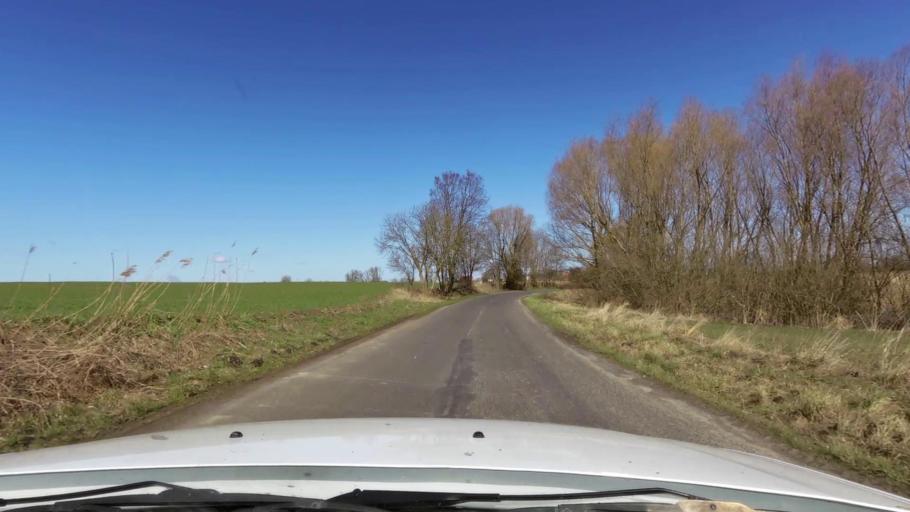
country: PL
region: West Pomeranian Voivodeship
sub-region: Powiat gryfinski
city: Cedynia
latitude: 52.8778
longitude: 14.2859
